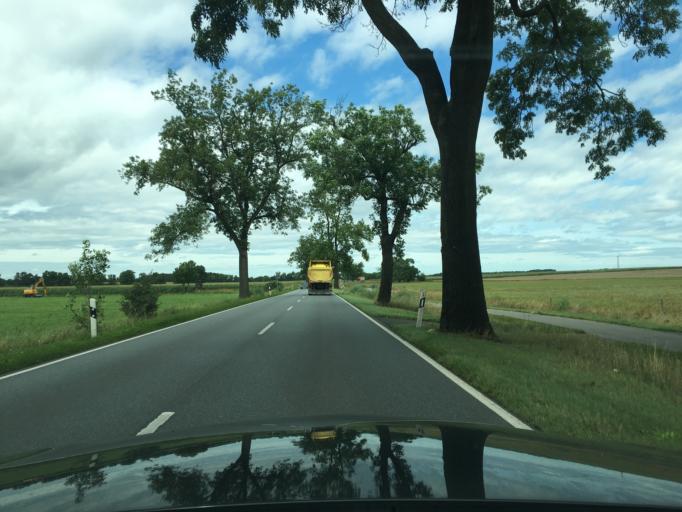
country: DE
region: Brandenburg
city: Gransee
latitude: 52.8730
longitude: 13.1645
